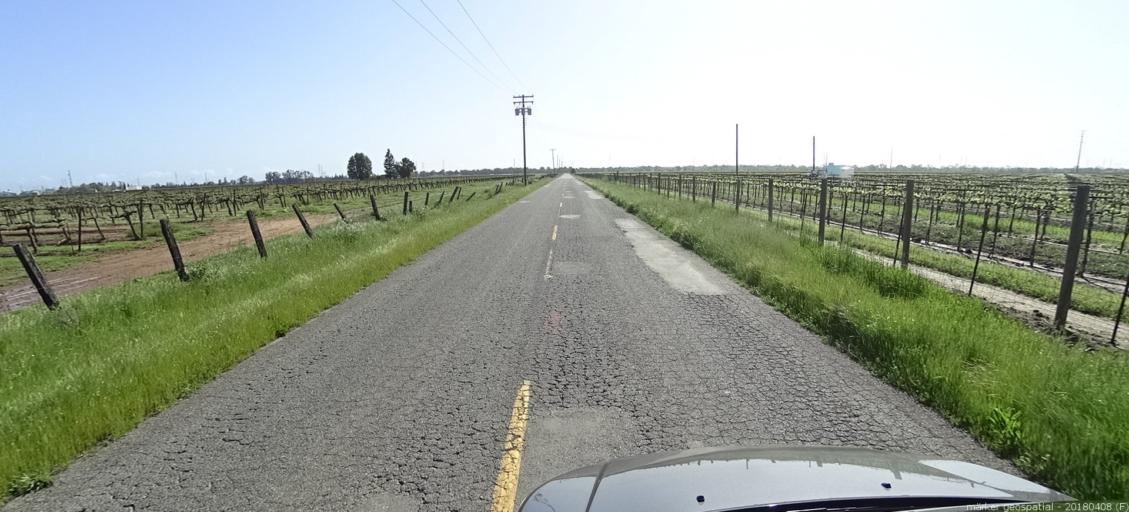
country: US
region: California
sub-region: Sacramento County
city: Elk Grove
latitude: 38.3617
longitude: -121.3677
